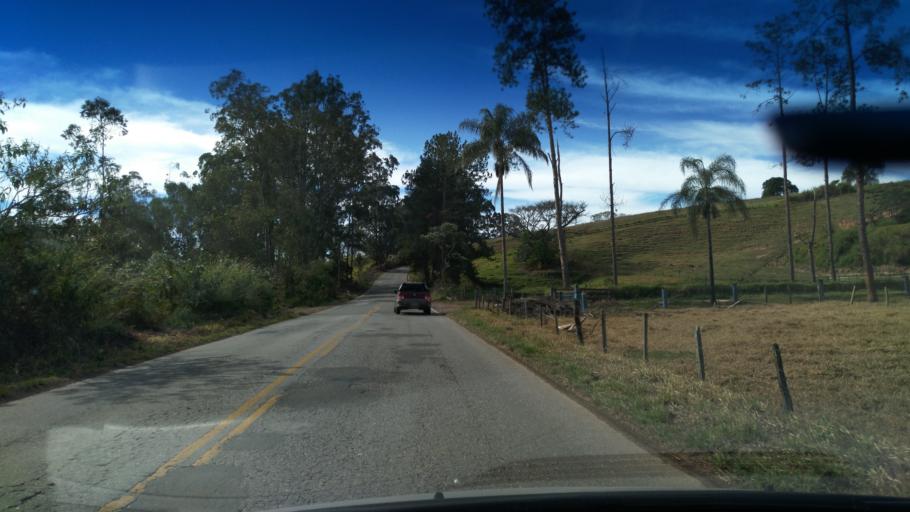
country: BR
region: Minas Gerais
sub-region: Andradas
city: Andradas
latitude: -22.0662
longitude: -46.4655
